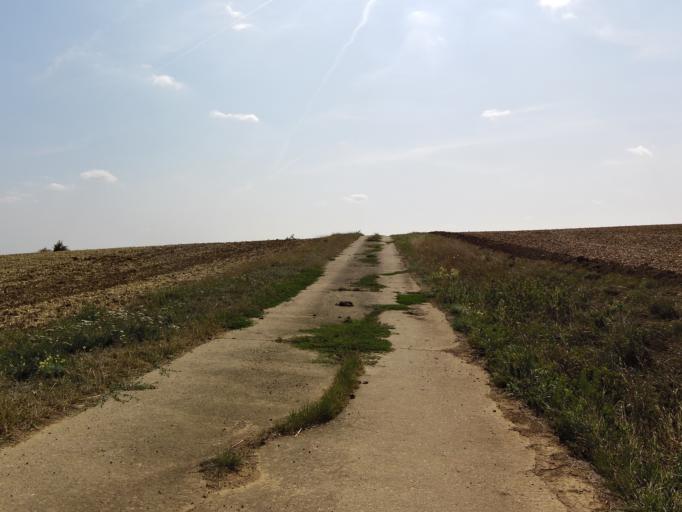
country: DE
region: Bavaria
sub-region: Regierungsbezirk Unterfranken
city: Theilheim
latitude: 49.7678
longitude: 10.0290
